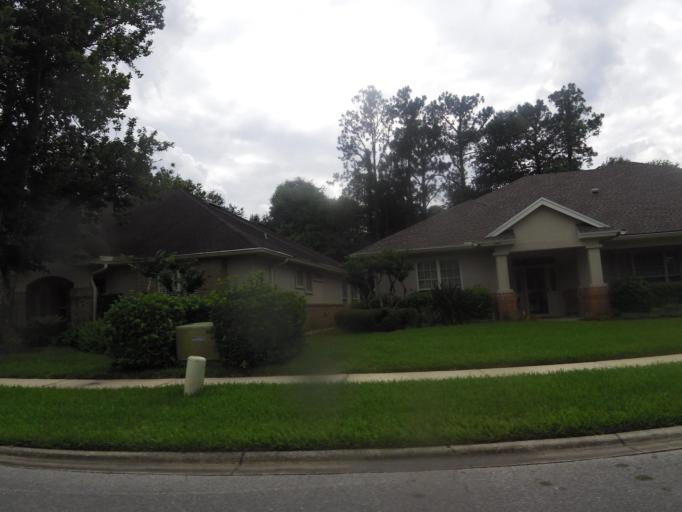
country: US
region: Florida
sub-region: Duval County
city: Jacksonville Beach
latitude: 30.2591
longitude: -81.4576
